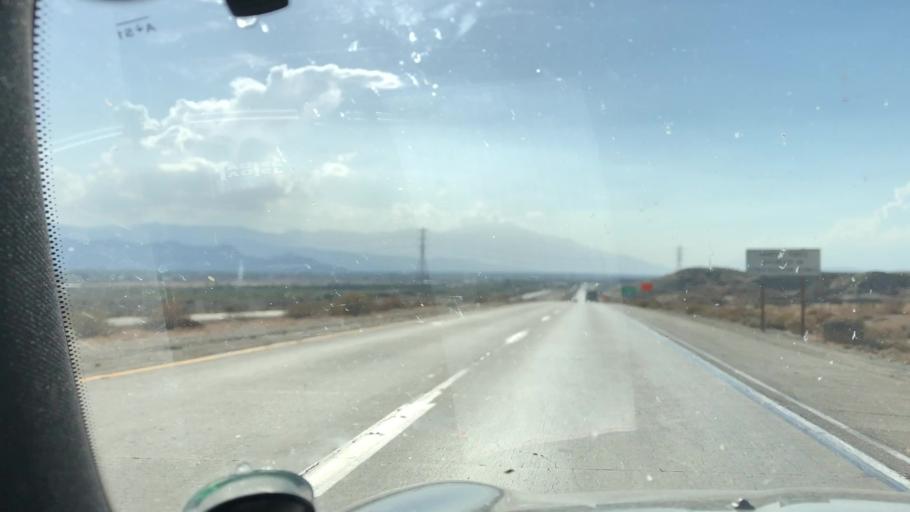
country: US
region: California
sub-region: Riverside County
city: Coachella
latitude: 33.7060
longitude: -116.1366
